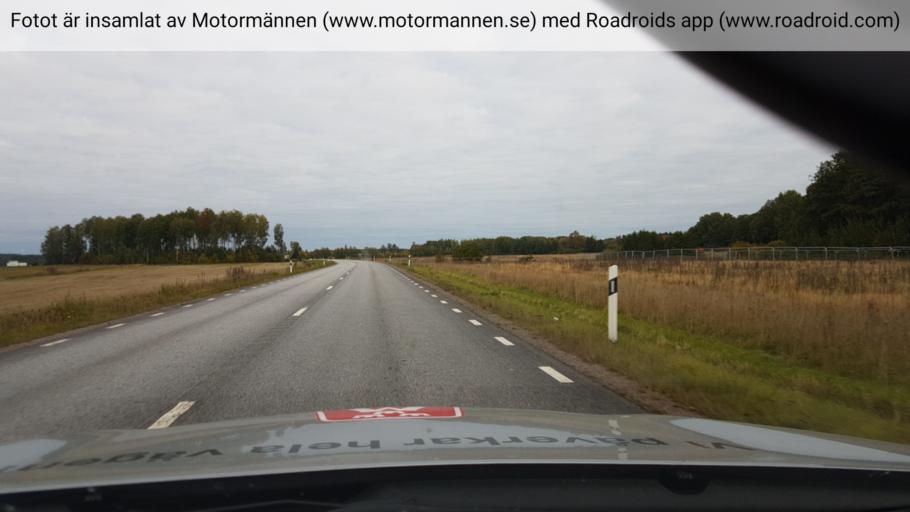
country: SE
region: Uppsala
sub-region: Tierps Kommun
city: Tierp
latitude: 60.3387
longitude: 17.5036
